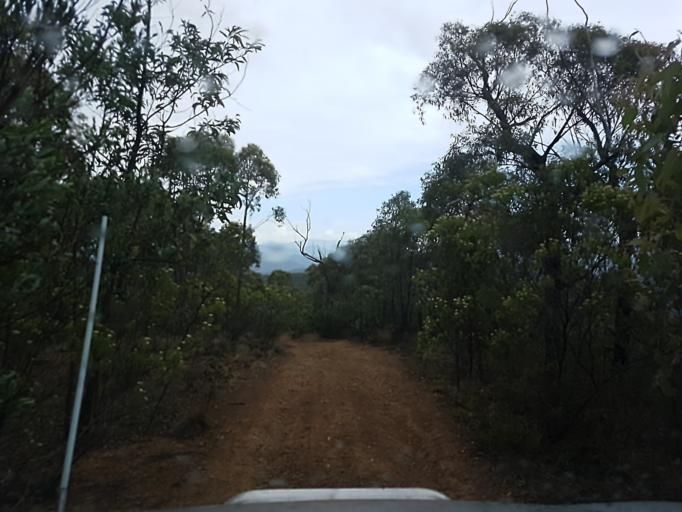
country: AU
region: New South Wales
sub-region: Snowy River
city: Jindabyne
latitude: -36.9140
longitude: 148.3360
